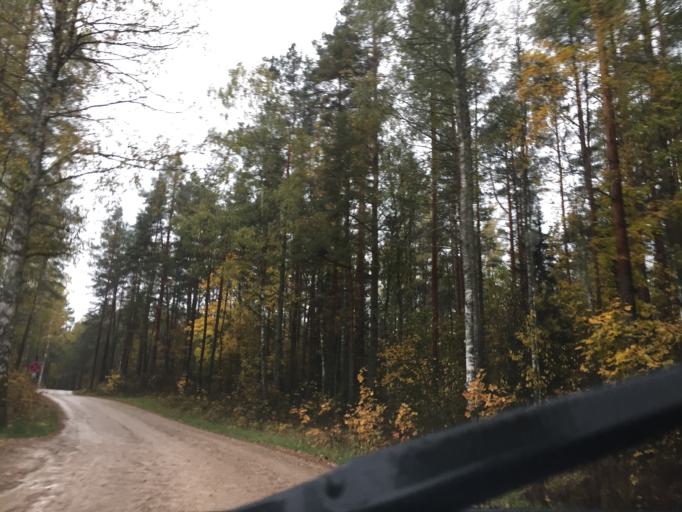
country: LV
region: Engure
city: Smarde
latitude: 56.9227
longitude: 23.4703
